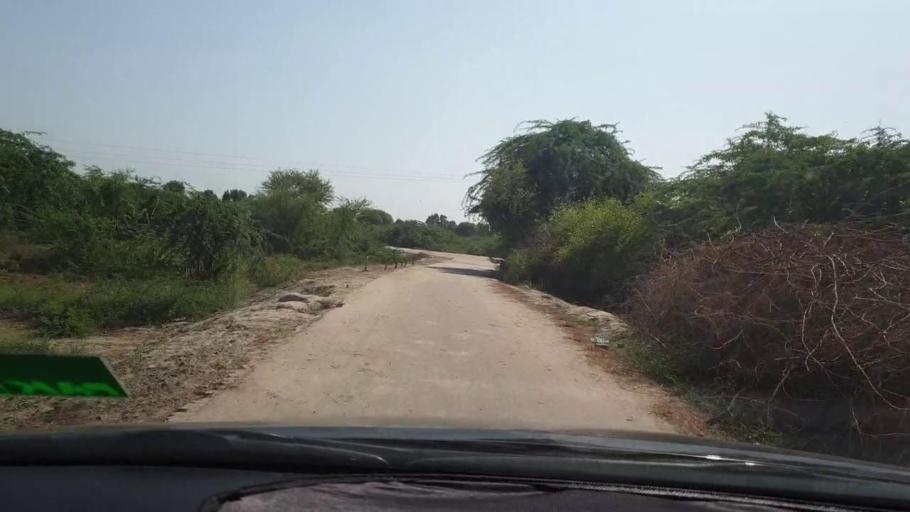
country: PK
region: Sindh
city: Naukot
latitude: 24.9357
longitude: 69.1877
